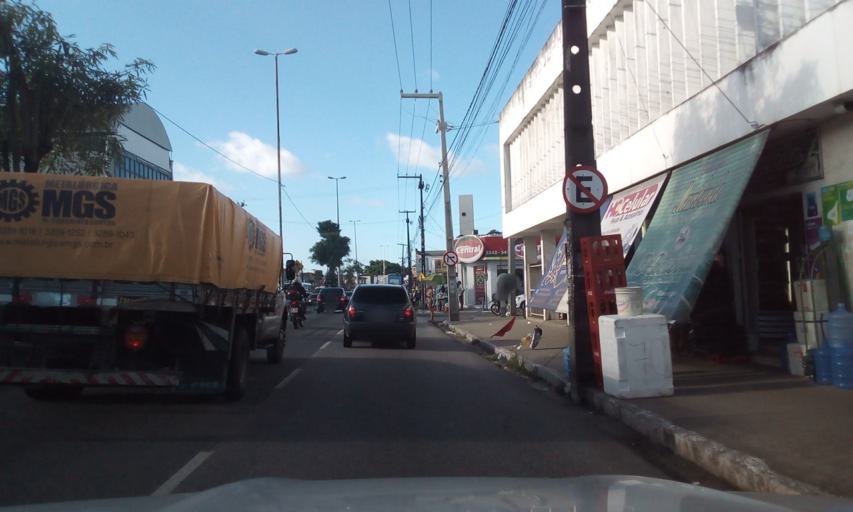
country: BR
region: Paraiba
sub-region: Joao Pessoa
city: Joao Pessoa
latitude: -7.1393
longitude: -34.8886
